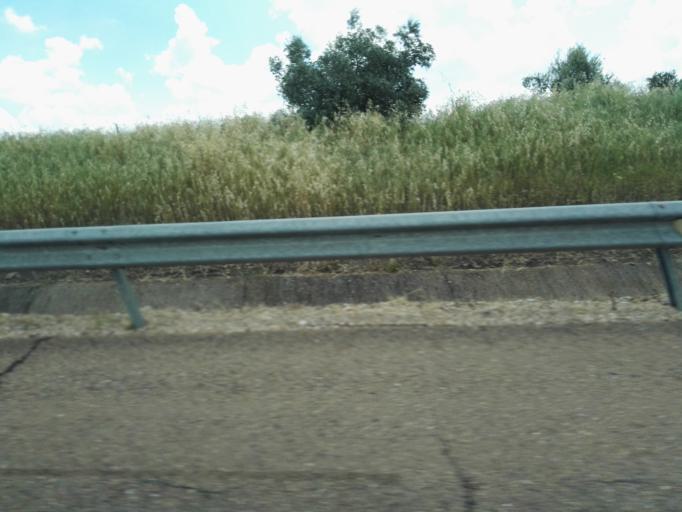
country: ES
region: Extremadura
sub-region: Provincia de Badajoz
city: Badajoz
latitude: 38.8964
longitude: -7.0048
